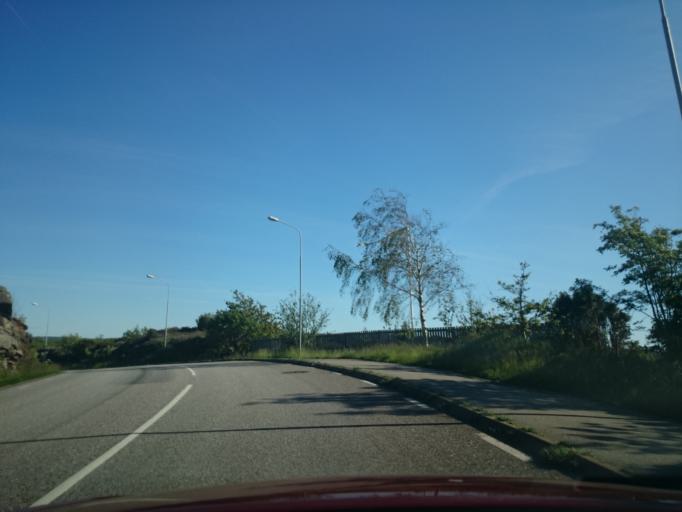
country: SE
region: Vaestra Goetaland
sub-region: Lysekils Kommun
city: Lysekil
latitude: 58.2456
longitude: 11.4654
